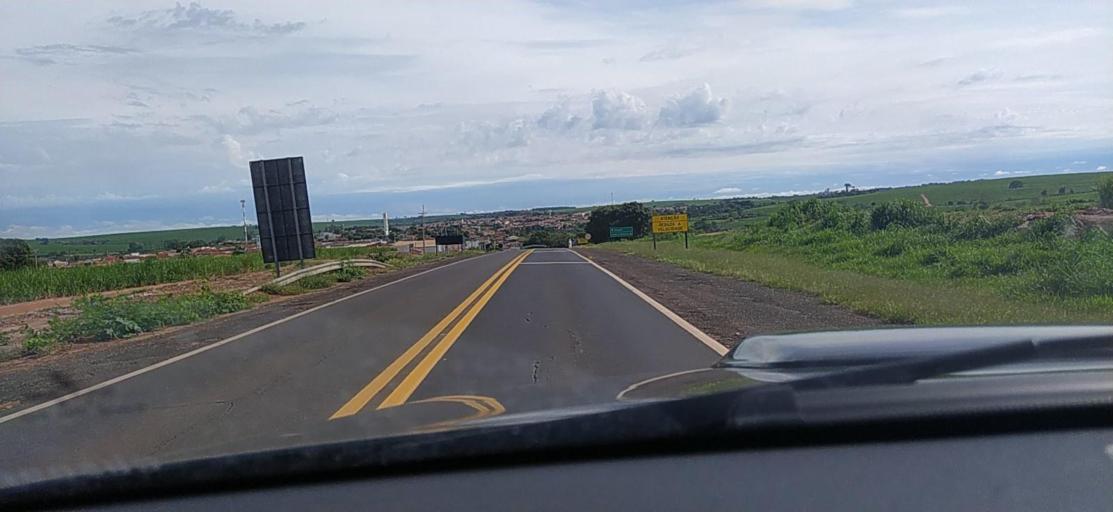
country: BR
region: Sao Paulo
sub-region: Catanduva
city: Catanduva
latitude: -21.0676
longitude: -49.0645
